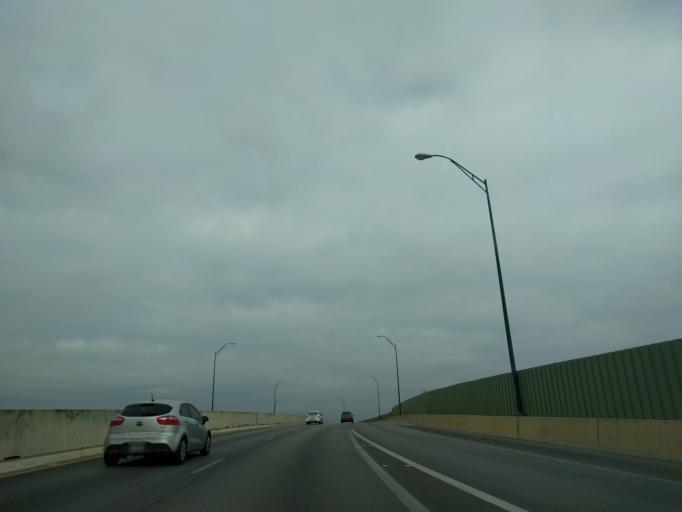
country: US
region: Texas
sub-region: Bexar County
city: Windcrest
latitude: 29.5429
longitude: -98.4257
